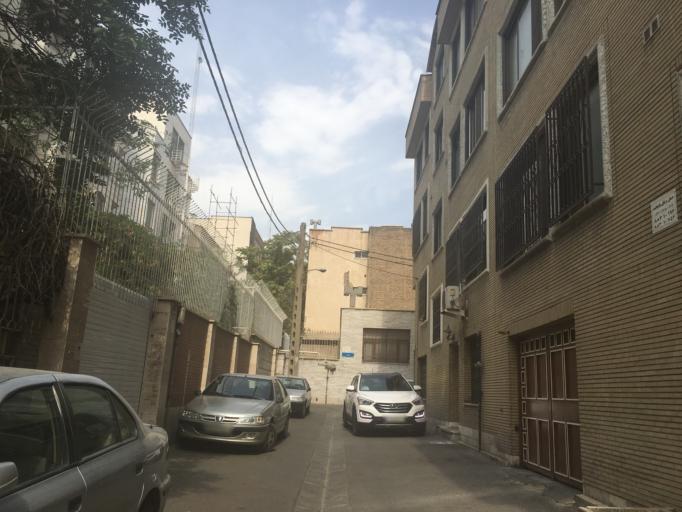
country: IR
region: Tehran
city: Tehran
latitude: 35.7345
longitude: 51.4439
